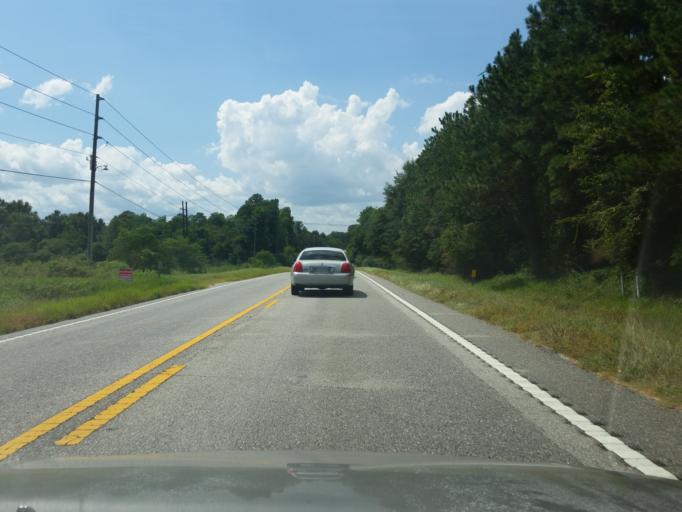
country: US
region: Alabama
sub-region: Baldwin County
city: Elberta
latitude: 30.5388
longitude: -87.5542
